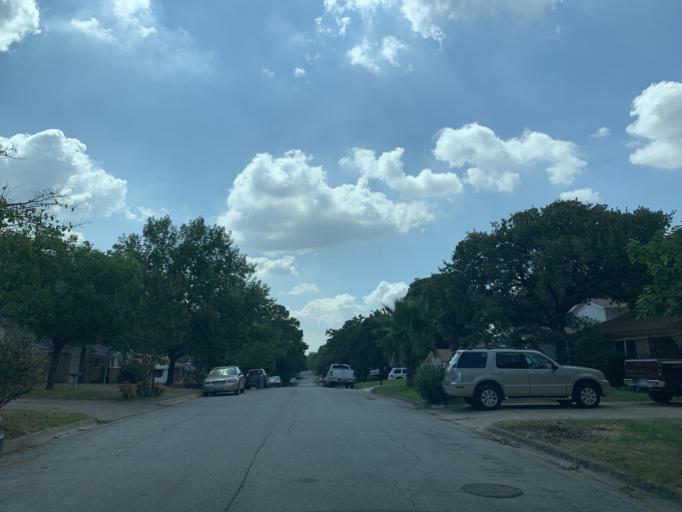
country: US
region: Texas
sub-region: Tarrant County
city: Azle
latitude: 32.8780
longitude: -97.5307
